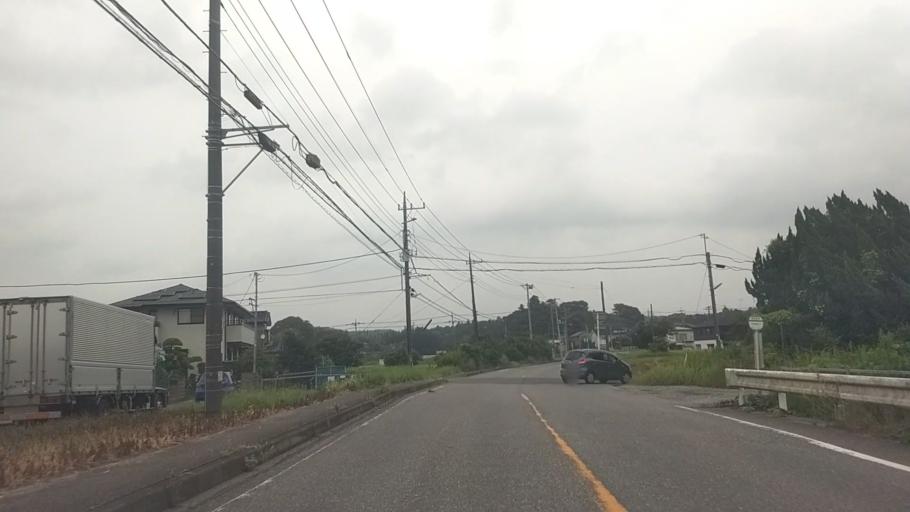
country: JP
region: Chiba
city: Kisarazu
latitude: 35.3880
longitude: 140.0465
